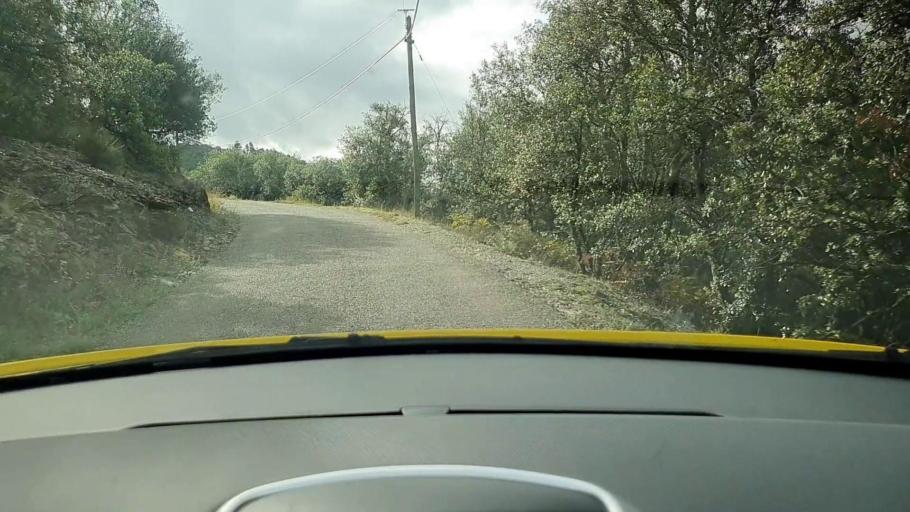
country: FR
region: Languedoc-Roussillon
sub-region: Departement du Gard
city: Sumene
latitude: 44.0166
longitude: 3.6640
